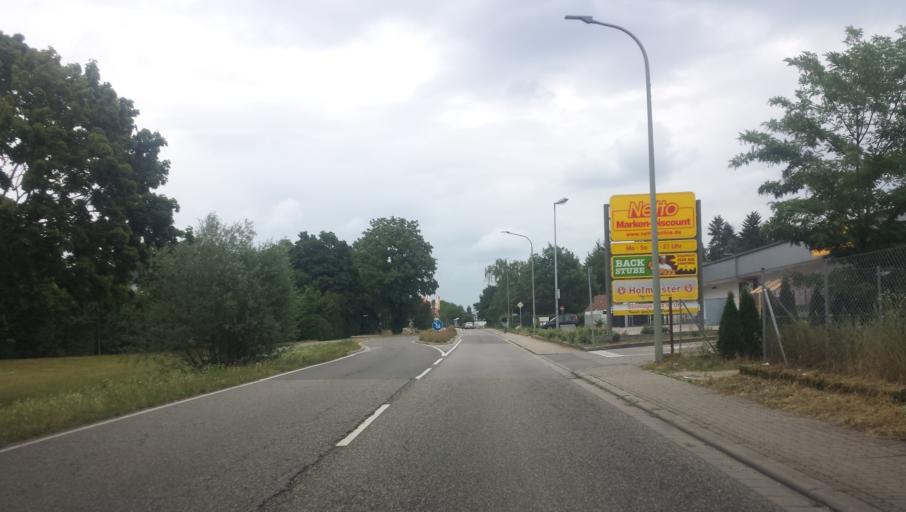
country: DE
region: Rheinland-Pfalz
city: Bellheim
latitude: 49.1933
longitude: 8.2928
